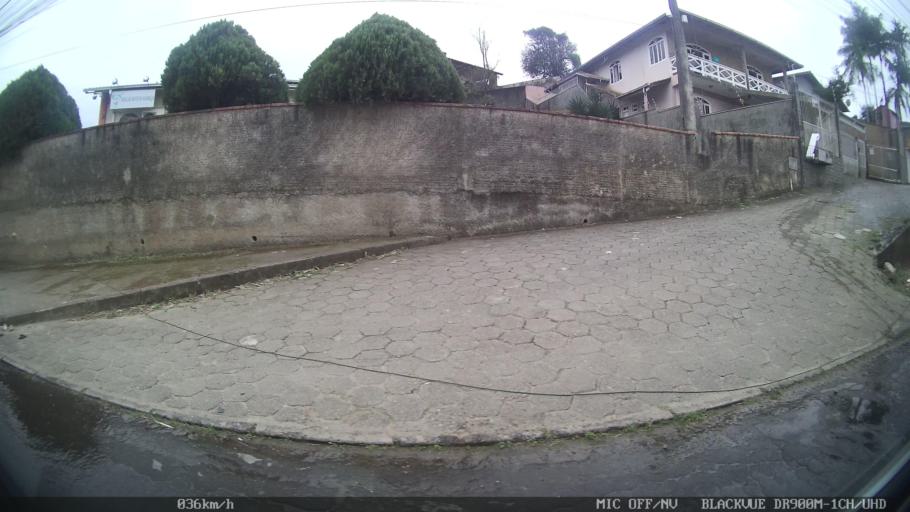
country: BR
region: Santa Catarina
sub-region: Joinville
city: Joinville
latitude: -26.3318
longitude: -48.8058
